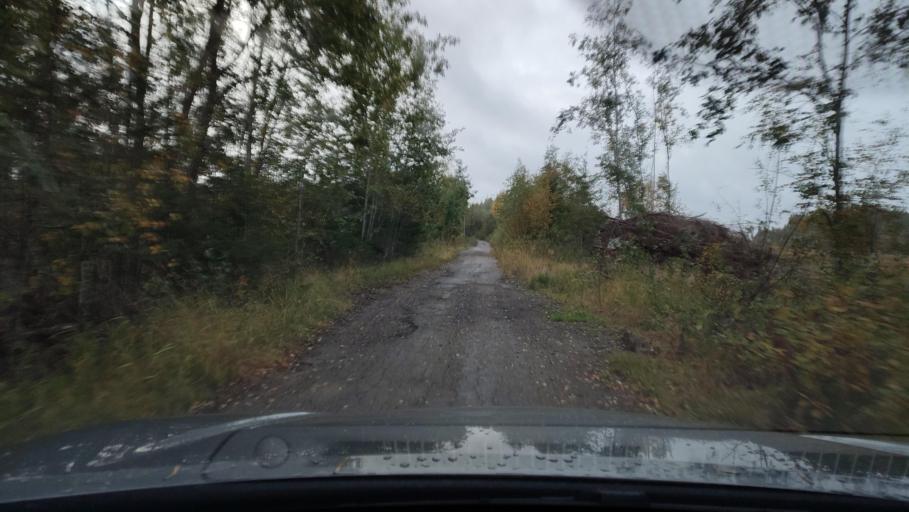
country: FI
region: Ostrobothnia
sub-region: Sydosterbotten
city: Kristinestad
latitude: 62.2672
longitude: 21.4591
